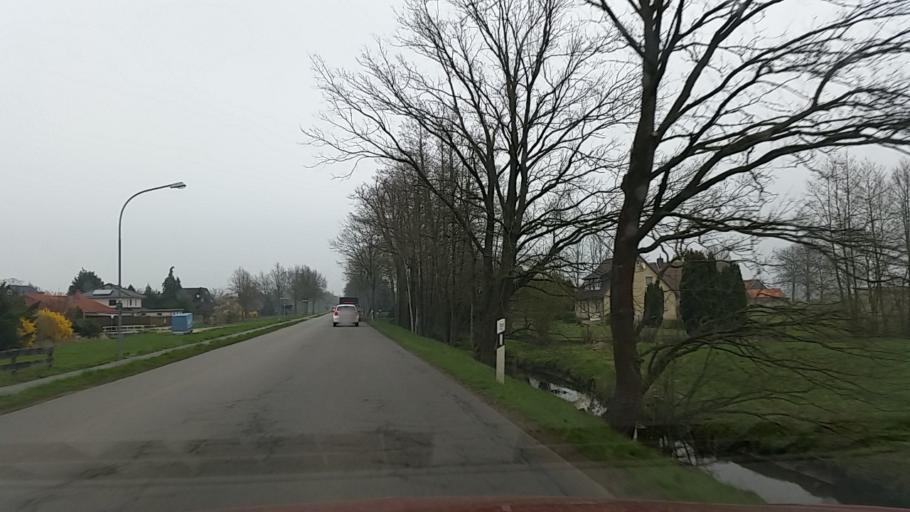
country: DE
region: Lower Saxony
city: Sassenburg
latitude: 52.5202
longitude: 10.5893
